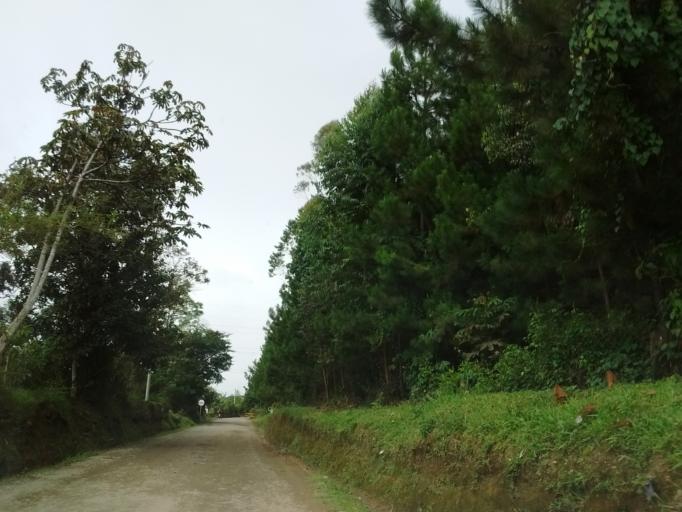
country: CO
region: Cauca
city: Popayan
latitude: 2.5267
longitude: -76.6021
